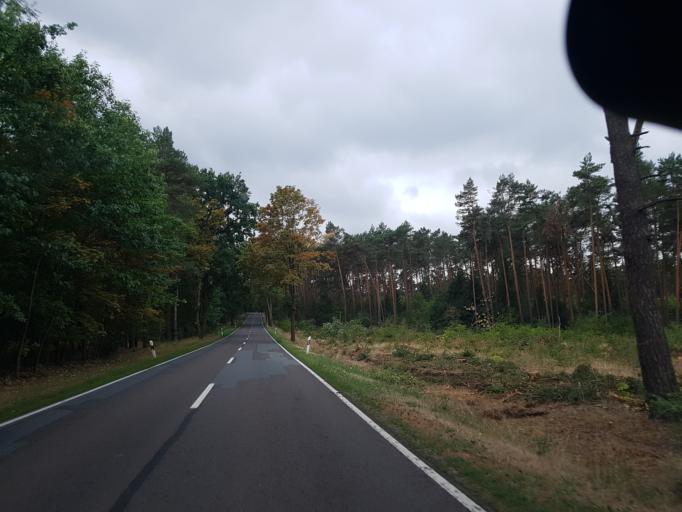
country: DE
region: Saxony-Anhalt
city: Loburg
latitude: 52.1458
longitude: 12.0946
